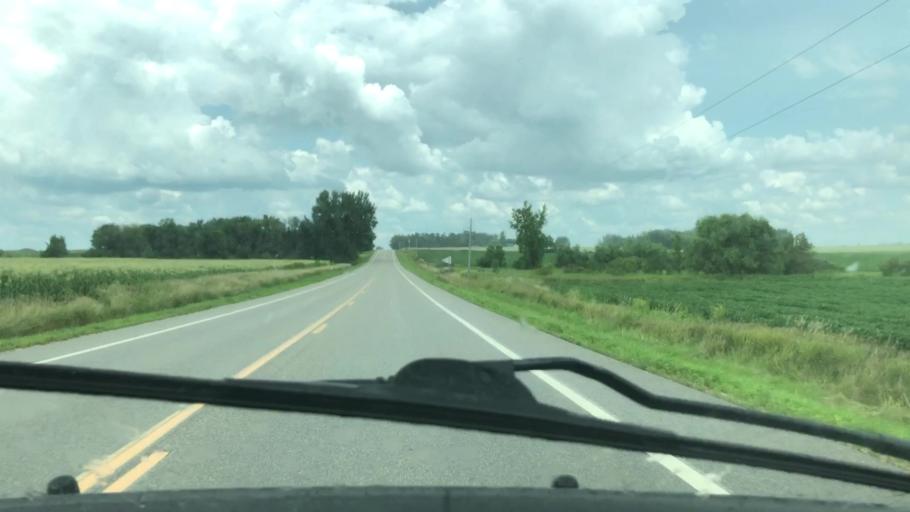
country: US
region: Minnesota
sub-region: Olmsted County
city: Stewartville
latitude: 43.8765
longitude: -92.5285
